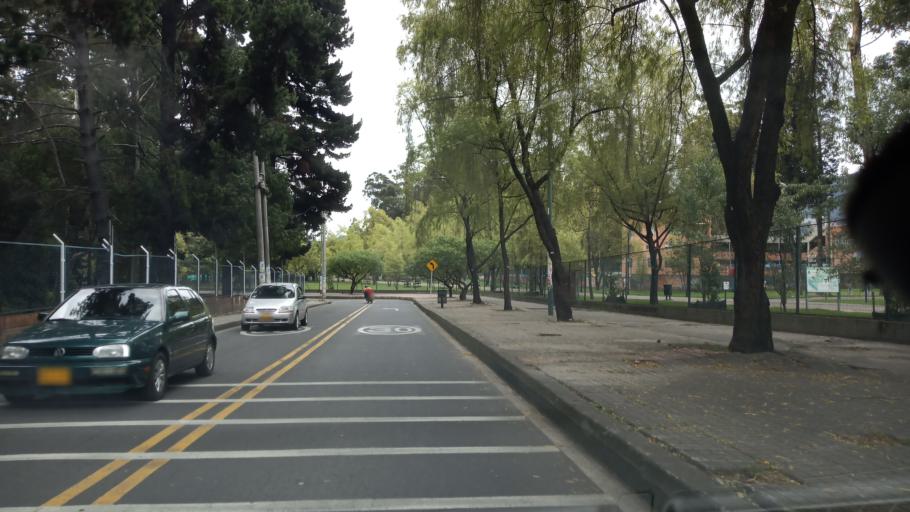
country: CO
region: Bogota D.C.
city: Bogota
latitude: 4.5706
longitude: -74.1060
